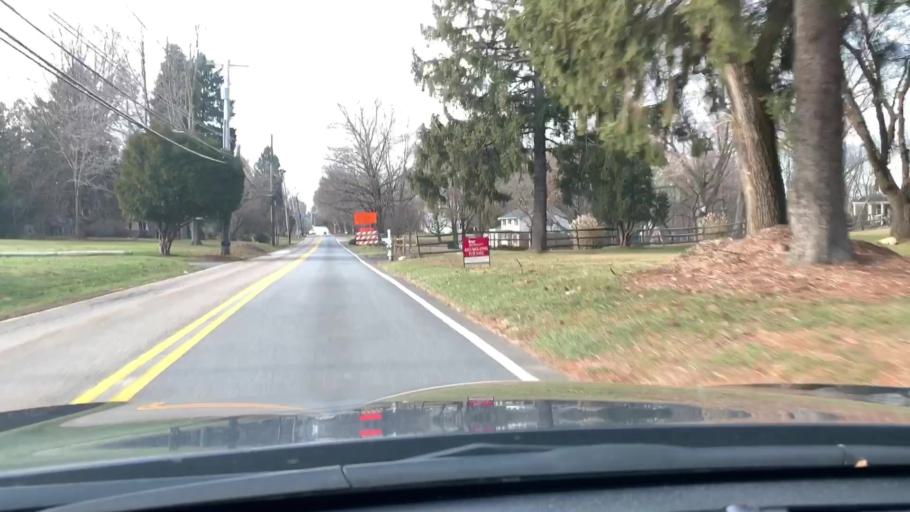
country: US
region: Pennsylvania
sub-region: Delaware County
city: Broomall
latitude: 39.9978
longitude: -75.3990
